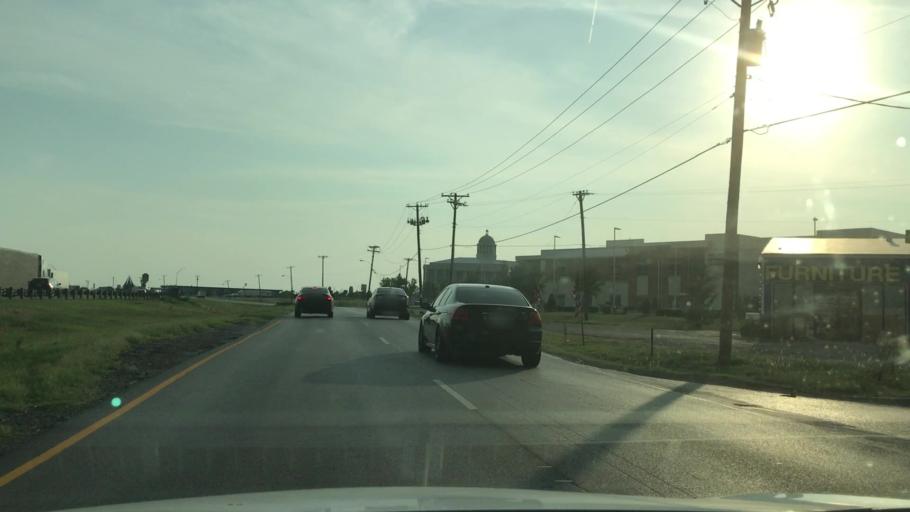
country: US
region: Texas
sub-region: Rockwall County
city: Rockwall
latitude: 32.9139
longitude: -96.4432
